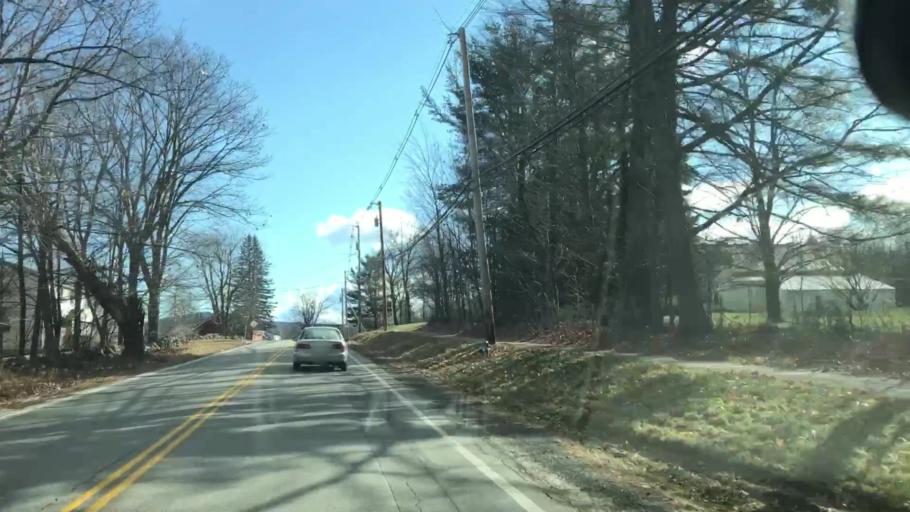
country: US
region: New Hampshire
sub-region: Carroll County
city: Wolfeboro
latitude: 43.5702
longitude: -71.1825
